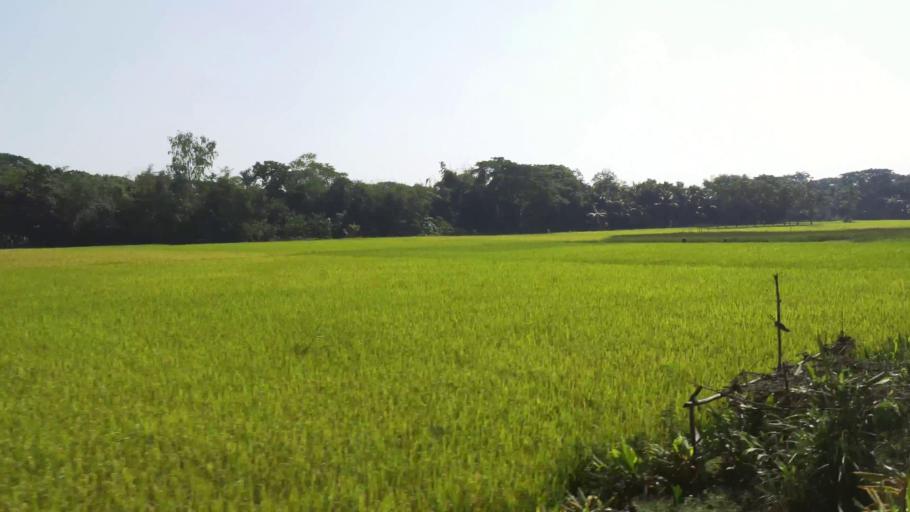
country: BD
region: Dhaka
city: Gafargaon
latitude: 24.5088
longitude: 90.5157
